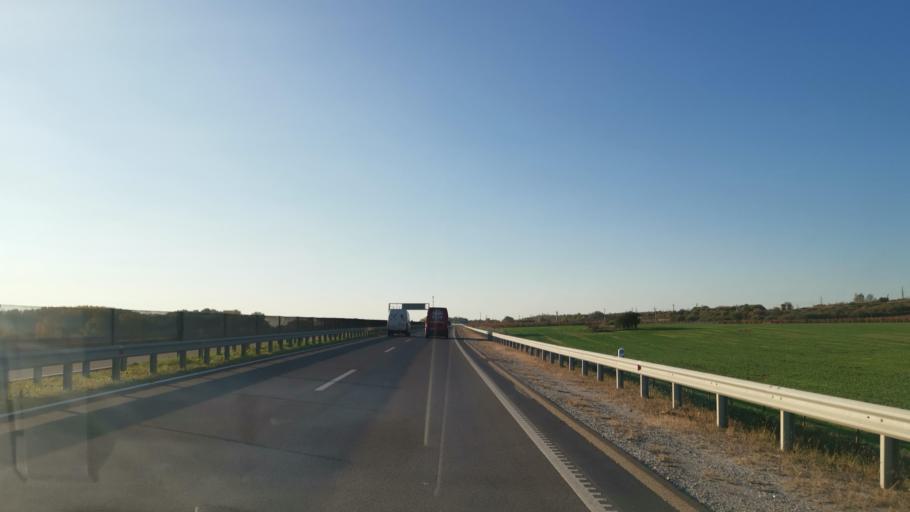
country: HU
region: Heves
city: Andornaktalya
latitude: 47.8610
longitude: 20.3965
